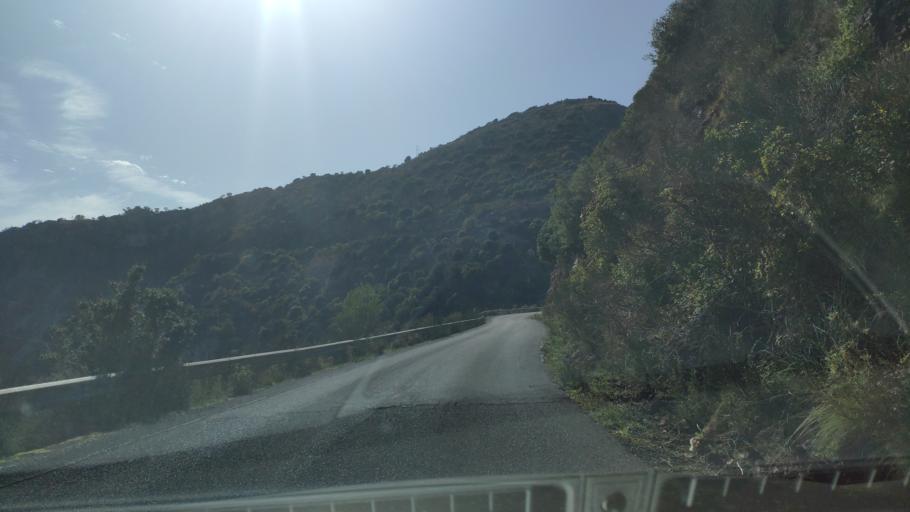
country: GR
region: Peloponnese
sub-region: Nomos Arkadias
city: Dimitsana
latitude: 37.5986
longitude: 22.0338
